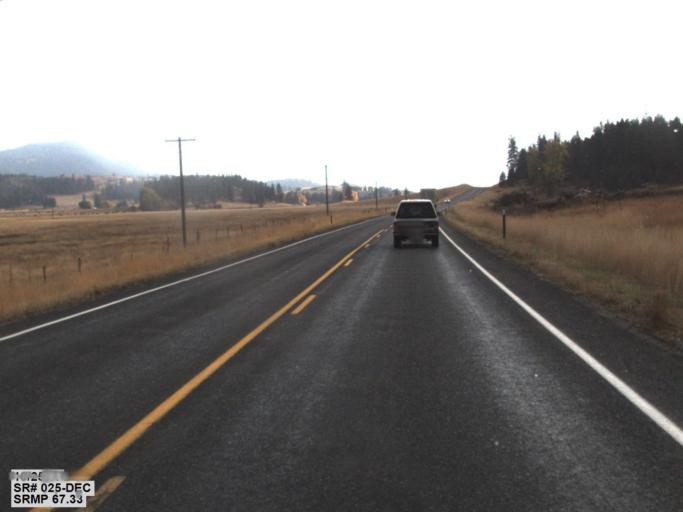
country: US
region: Washington
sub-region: Stevens County
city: Kettle Falls
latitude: 48.4432
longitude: -118.1705
